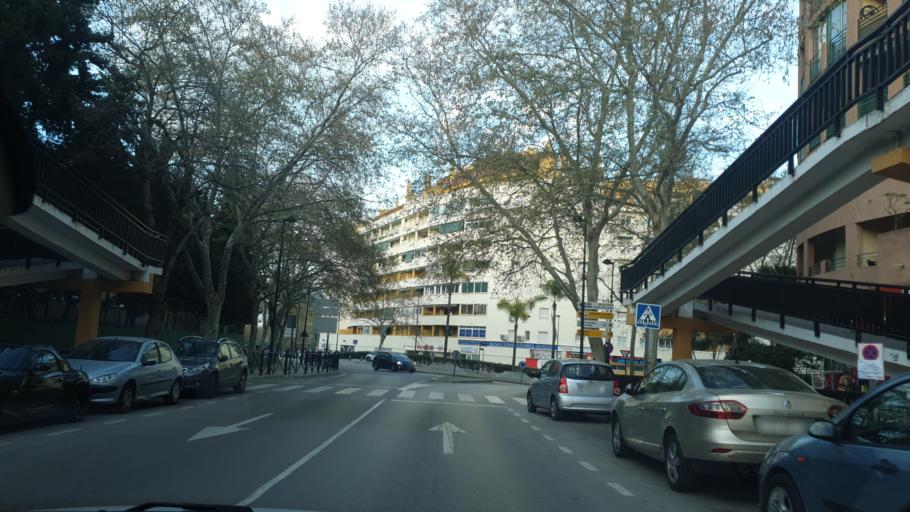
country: ES
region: Andalusia
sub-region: Provincia de Malaga
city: Marbella
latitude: 36.5166
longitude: -4.8932
